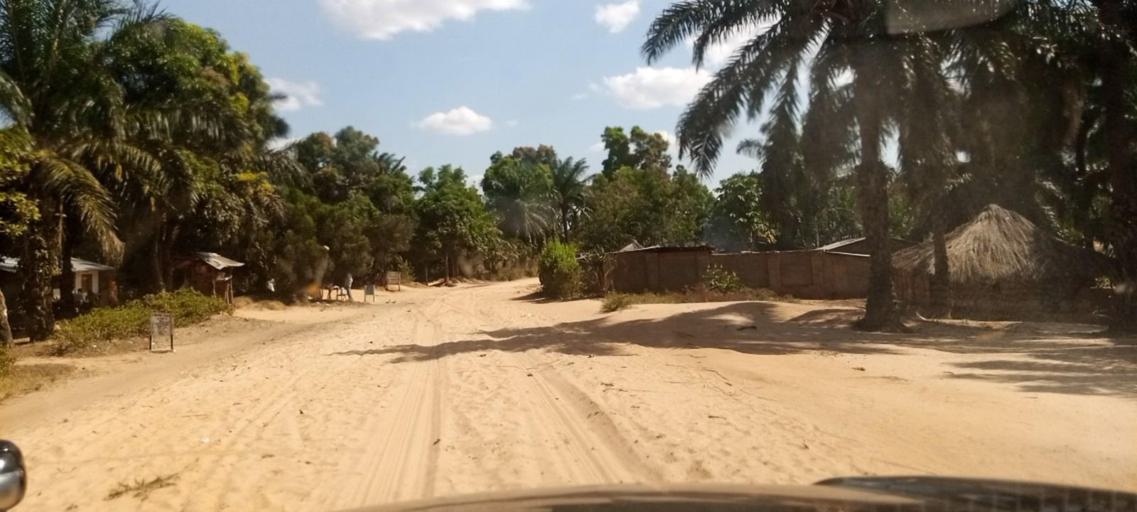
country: CD
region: Kasai-Oriental
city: Kabinda
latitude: -6.1329
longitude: 24.5124
